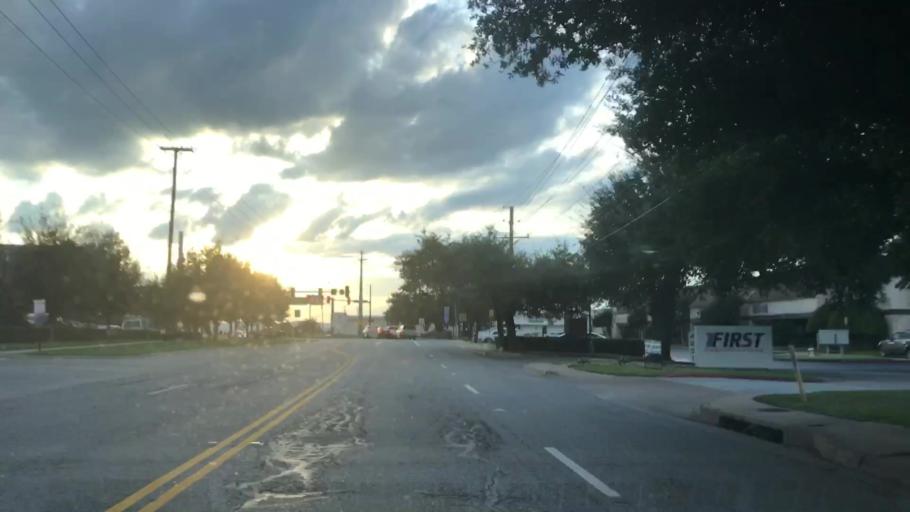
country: US
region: Texas
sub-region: Dallas County
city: Addison
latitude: 32.9687
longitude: -96.8285
